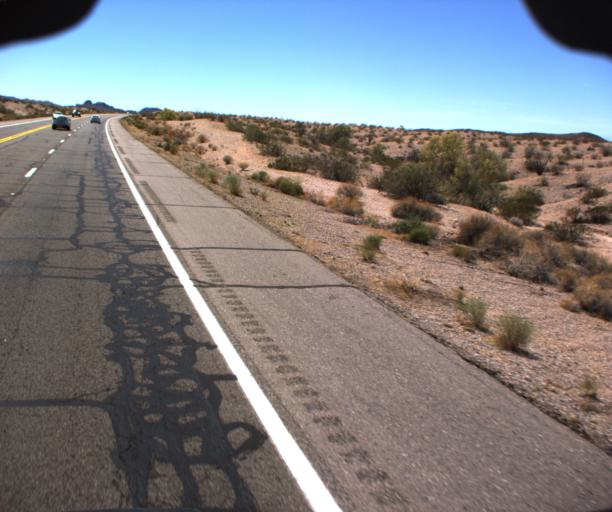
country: US
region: Arizona
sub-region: Mohave County
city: Desert Hills
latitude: 34.6942
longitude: -114.3017
